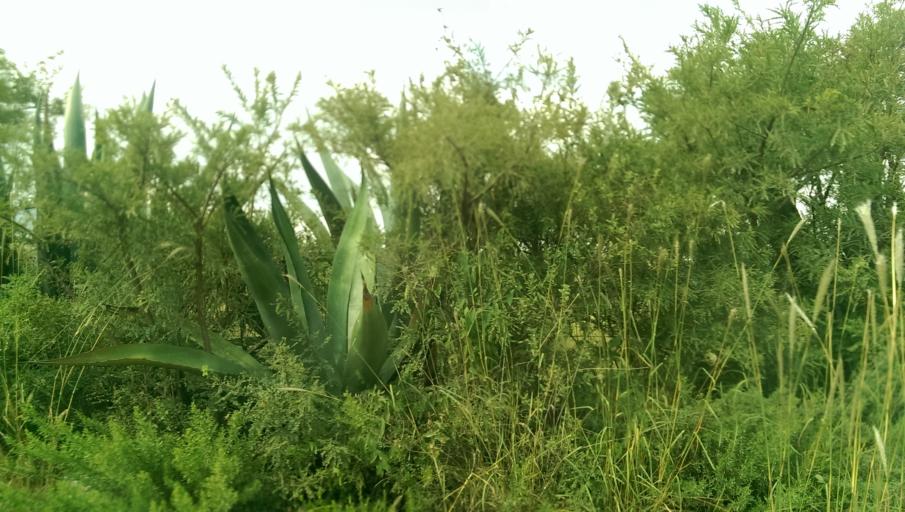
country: MX
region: Queretaro
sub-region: Huimilpan
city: San Jose Tepuzas
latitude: 20.3565
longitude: -100.3956
